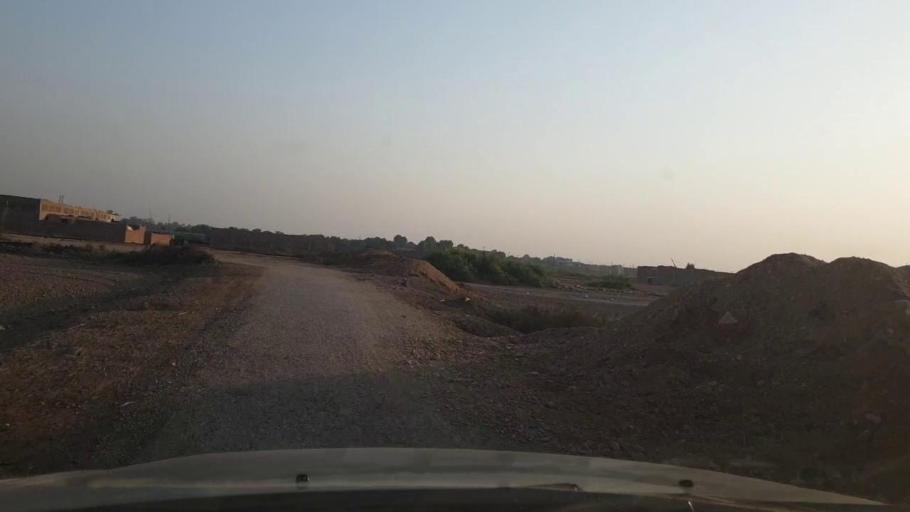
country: PK
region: Sindh
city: Tando Jam
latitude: 25.4253
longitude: 68.5080
